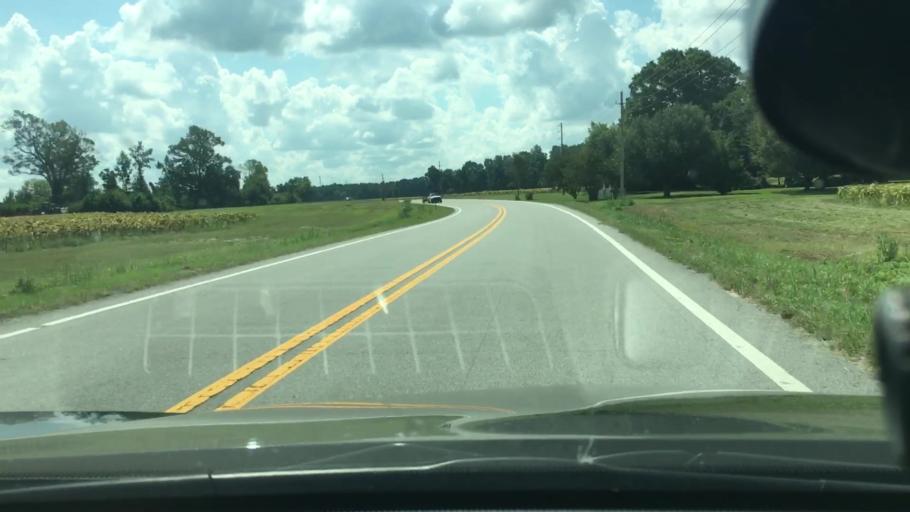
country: US
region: North Carolina
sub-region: Pitt County
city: Farmville
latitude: 35.6778
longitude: -77.4893
